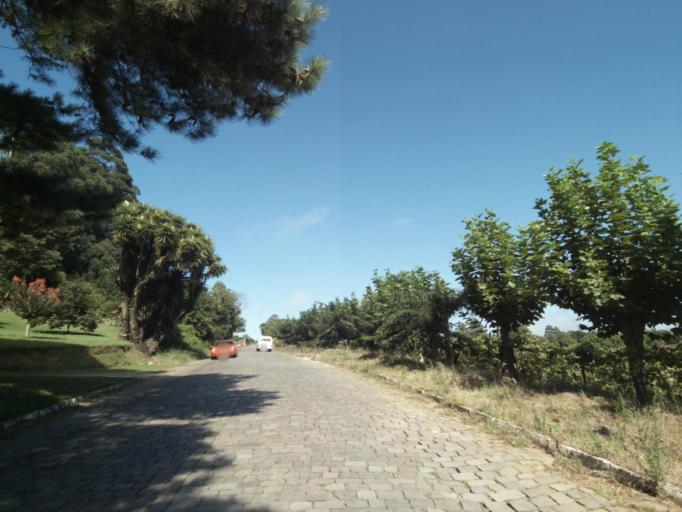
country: BR
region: Rio Grande do Sul
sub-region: Bento Goncalves
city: Bento Goncalves
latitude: -29.1187
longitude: -51.5626
